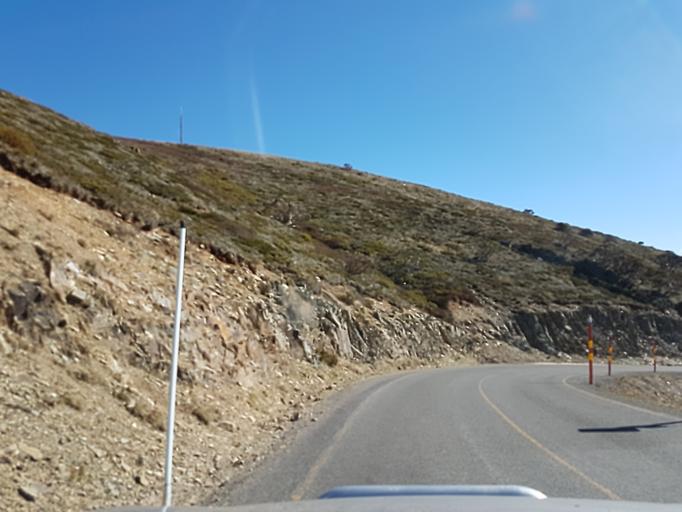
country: AU
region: Victoria
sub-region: Alpine
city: Mount Beauty
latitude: -36.9733
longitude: 147.1287
